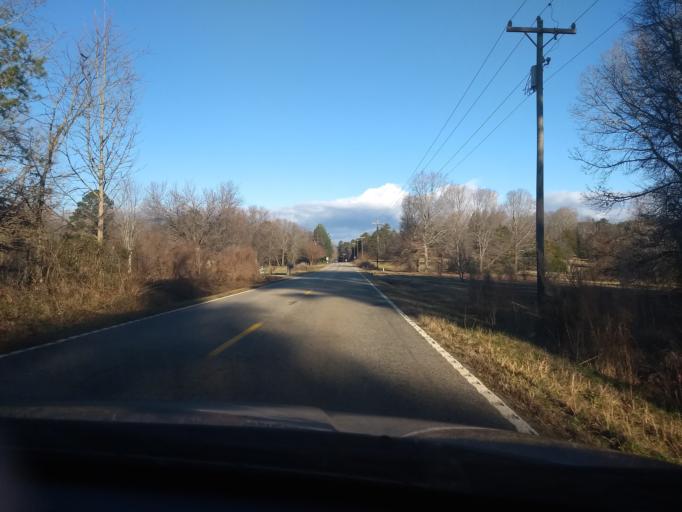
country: US
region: South Carolina
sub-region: Greenville County
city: Greer
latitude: 35.0038
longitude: -82.2142
